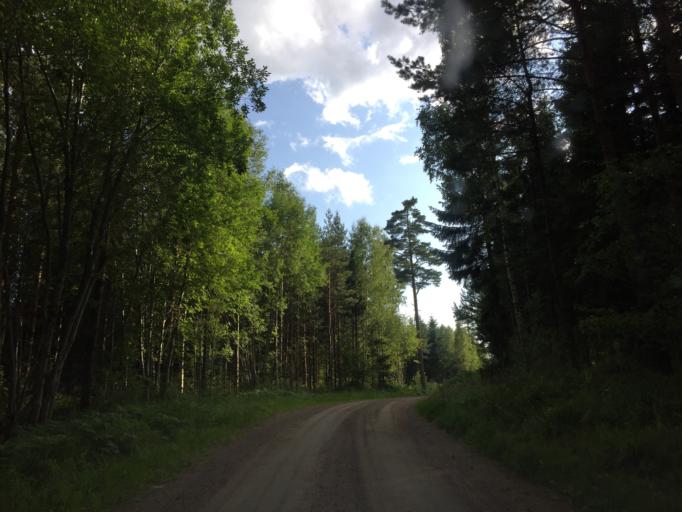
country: SE
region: OEstergoetland
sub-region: Motala Kommun
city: Ryd
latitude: 58.7003
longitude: 15.0314
